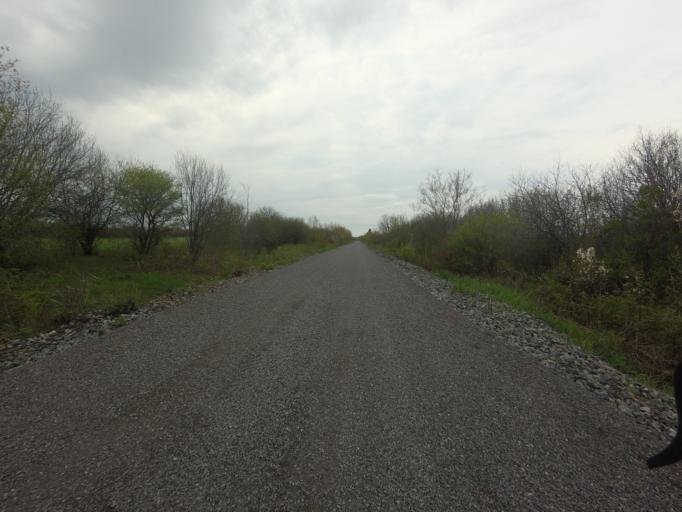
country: CA
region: Ontario
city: Carleton Place
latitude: 45.2141
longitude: -76.1804
